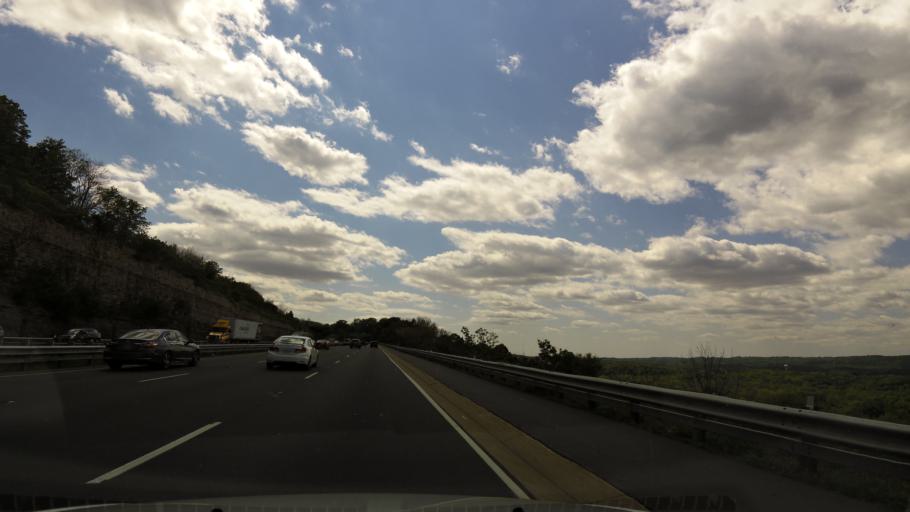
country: CA
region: Ontario
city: Ancaster
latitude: 43.2442
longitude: -79.9418
